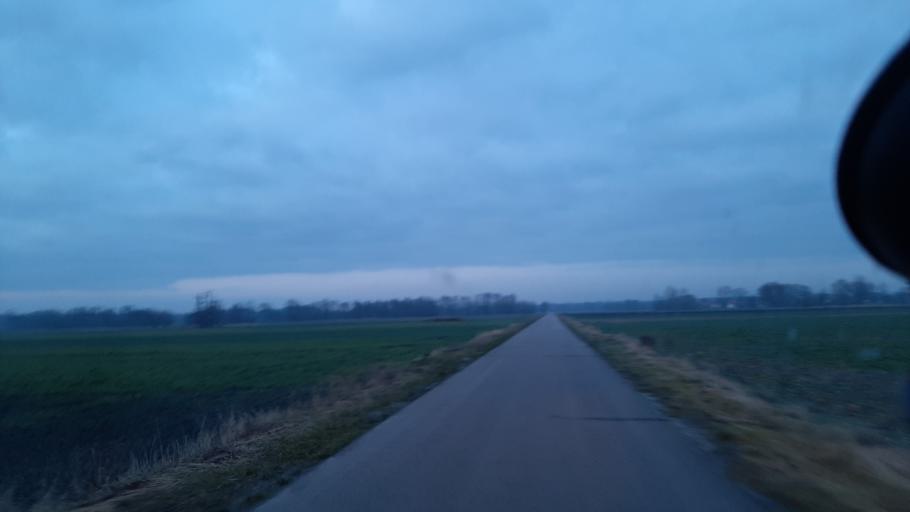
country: PL
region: Lublin Voivodeship
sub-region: Powiat lubartowski
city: Firlej
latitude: 51.5784
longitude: 22.5393
